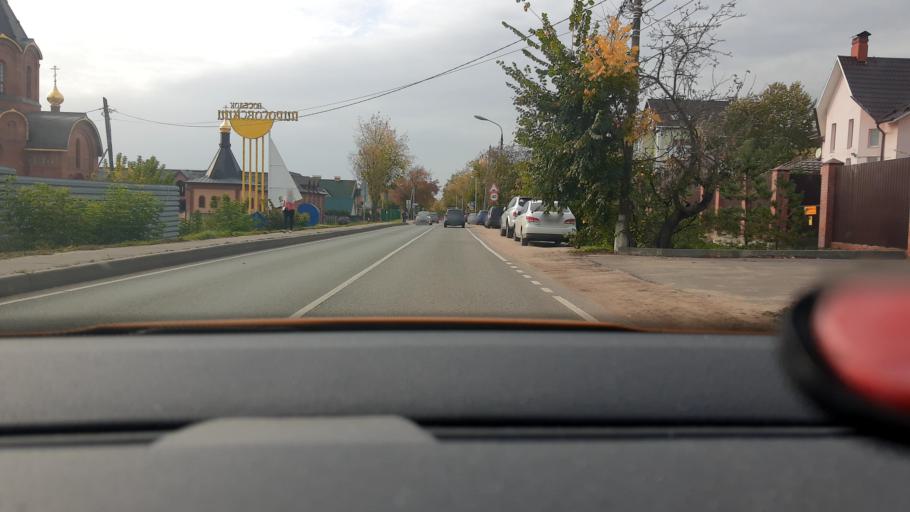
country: RU
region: Moskovskaya
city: Pirogovskiy
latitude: 55.9800
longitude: 37.7349
